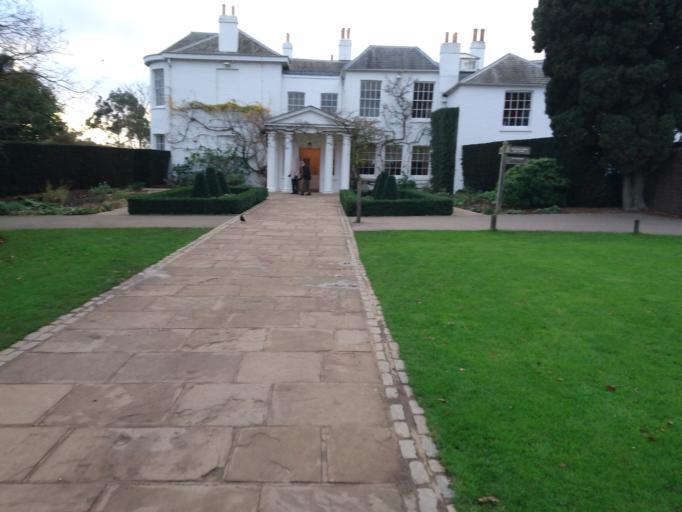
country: GB
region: England
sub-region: Greater London
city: Richmond
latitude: 51.4426
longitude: -0.2939
